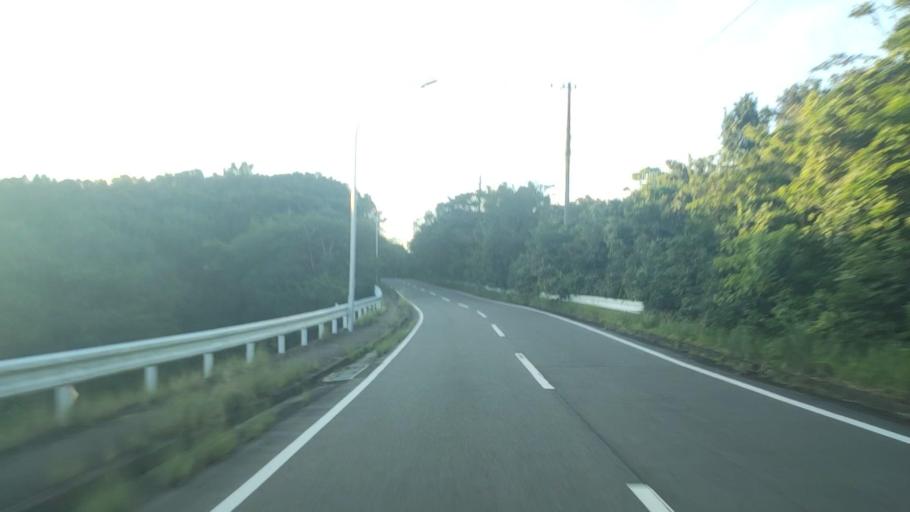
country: JP
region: Mie
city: Toba
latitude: 34.3131
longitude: 136.8163
